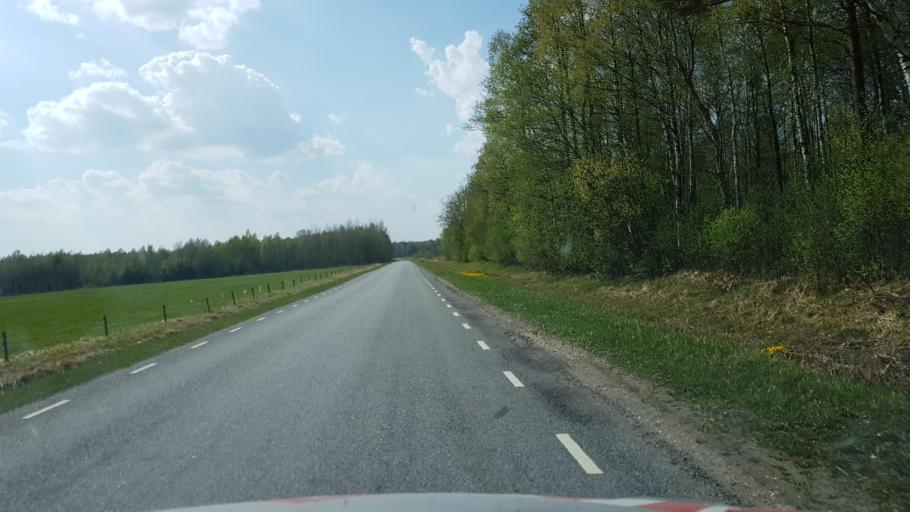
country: EE
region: Paernumaa
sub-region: Sauga vald
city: Sauga
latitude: 58.4401
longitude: 24.5738
